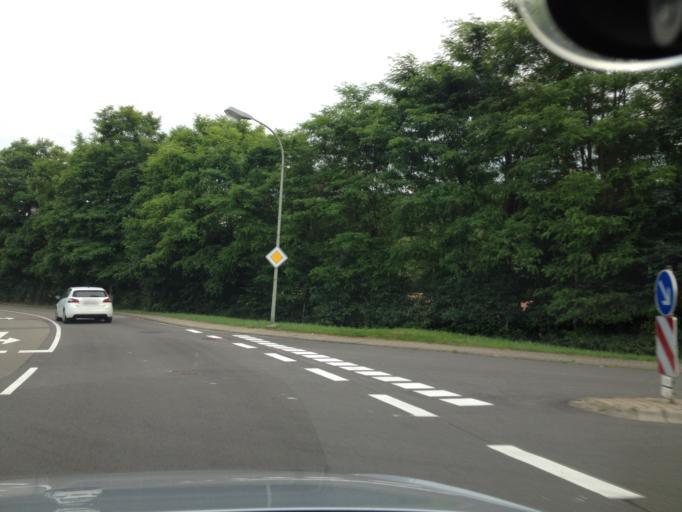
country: DE
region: Saarland
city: Friedrichsthal
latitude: 49.3541
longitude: 7.0937
